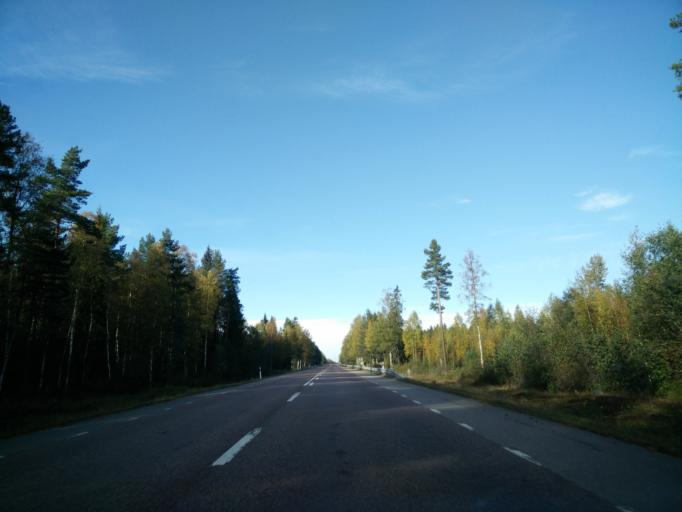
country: SE
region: Gaevleborg
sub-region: Hudiksvalls Kommun
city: Iggesund
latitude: 61.5784
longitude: 17.0267
